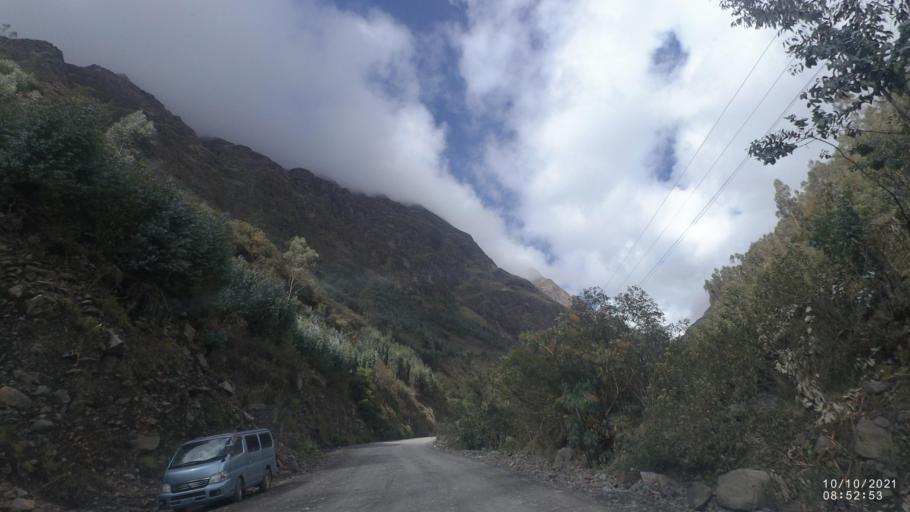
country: BO
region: La Paz
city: Quime
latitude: -16.9867
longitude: -67.2303
